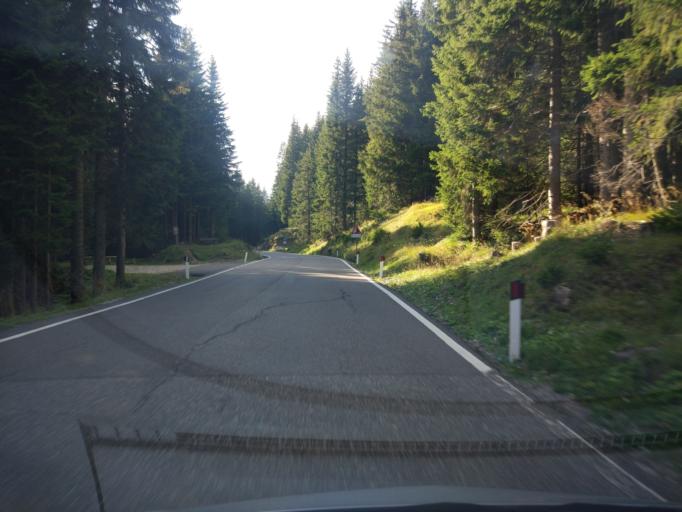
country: IT
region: Veneto
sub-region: Provincia di Belluno
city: Falcade Alto
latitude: 46.2956
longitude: 11.7692
